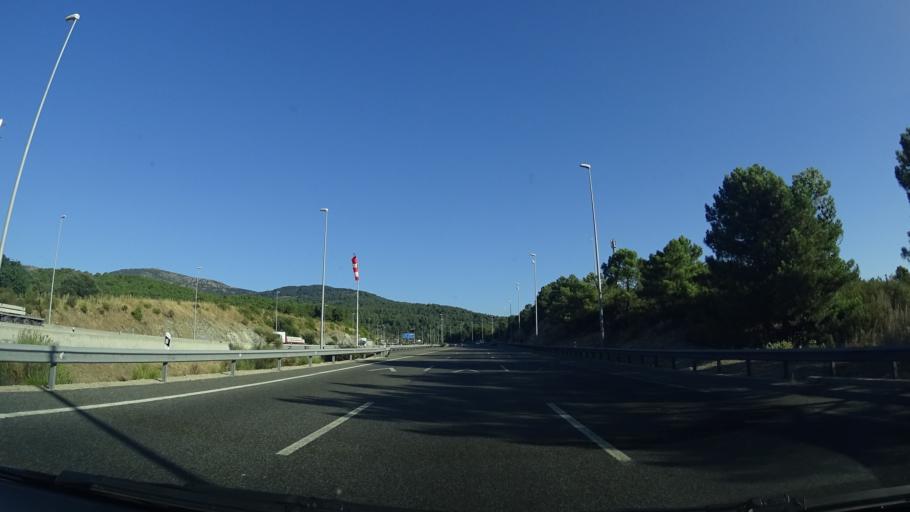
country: ES
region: Madrid
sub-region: Provincia de Madrid
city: Guadarrama
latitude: 40.6730
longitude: -4.1118
